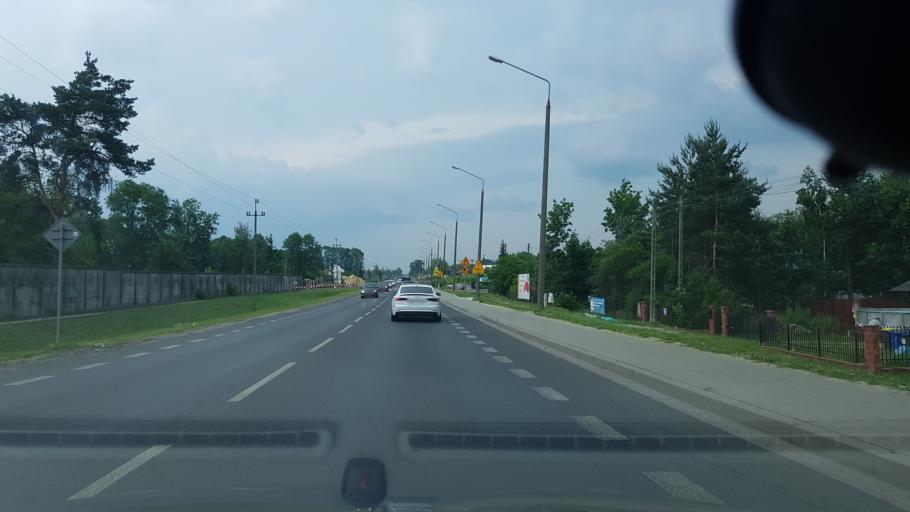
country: PL
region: Masovian Voivodeship
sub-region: Powiat legionowski
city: Michalow-Reginow
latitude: 52.4098
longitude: 20.9569
